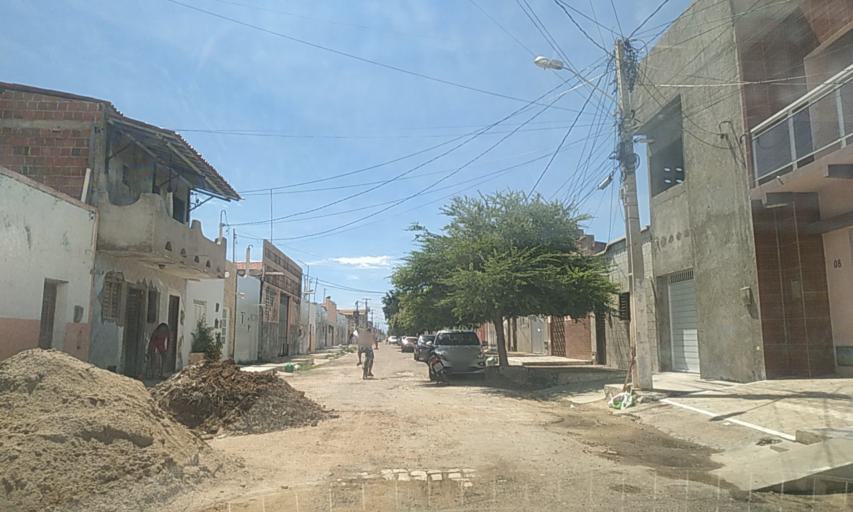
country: BR
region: Rio Grande do Norte
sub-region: Areia Branca
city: Areia Branca
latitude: -4.9604
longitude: -37.1342
